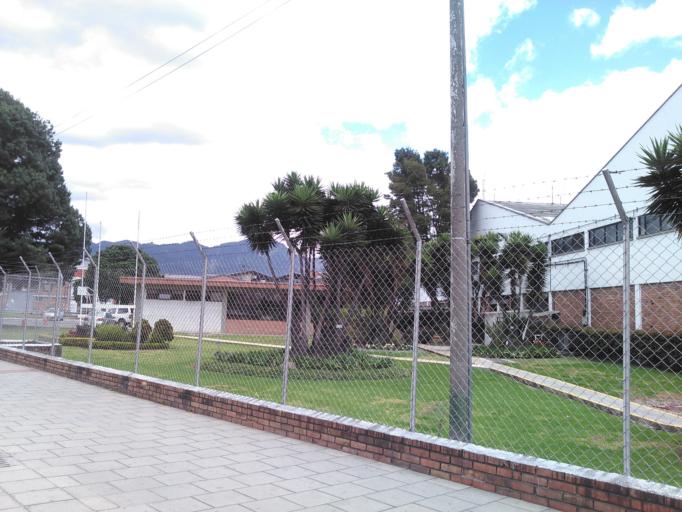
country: CO
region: Bogota D.C.
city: Bogota
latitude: 4.6277
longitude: -74.1142
